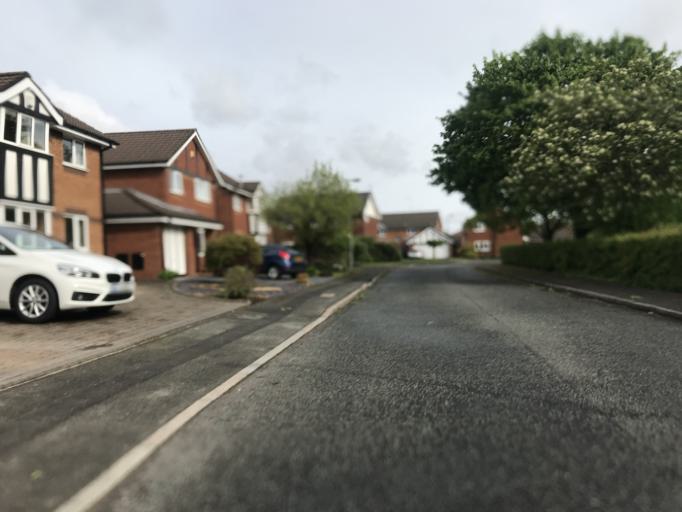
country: GB
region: England
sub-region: Borough of Stockport
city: Cheadle Heath
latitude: 53.4156
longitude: -2.1850
